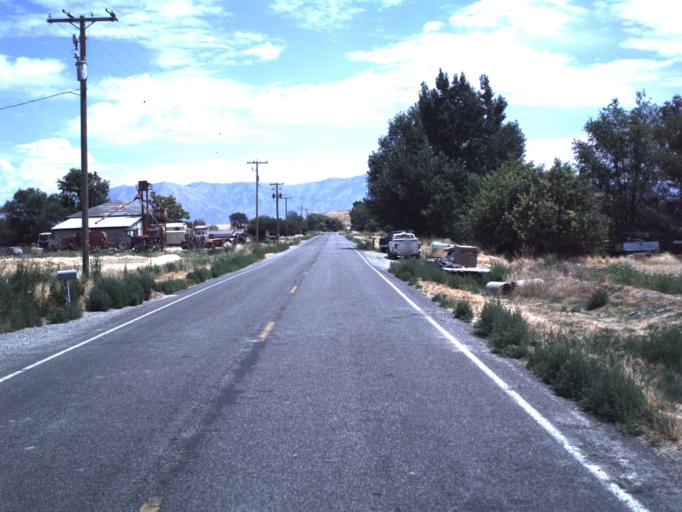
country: US
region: Utah
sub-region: Box Elder County
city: Tremonton
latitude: 41.6508
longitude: -112.3034
